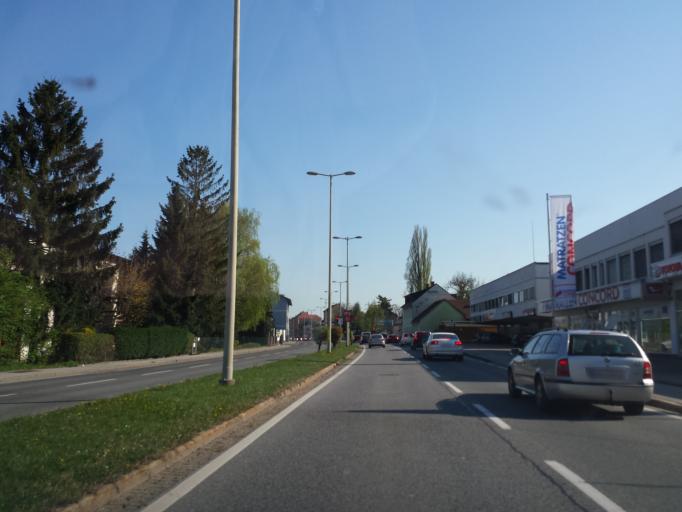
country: AT
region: Styria
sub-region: Graz Stadt
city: Goesting
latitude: 47.0976
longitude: 15.4038
